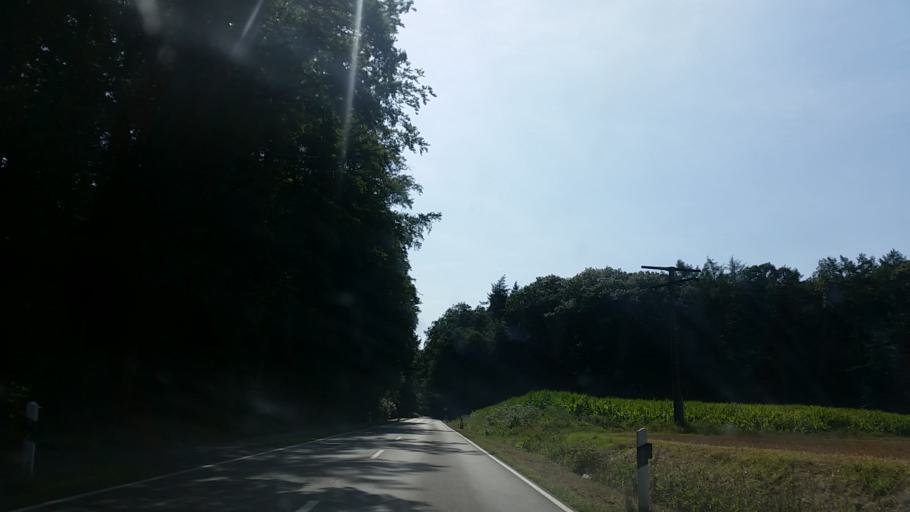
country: DE
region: Lower Saxony
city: Ankum
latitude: 52.5237
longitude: 7.8981
